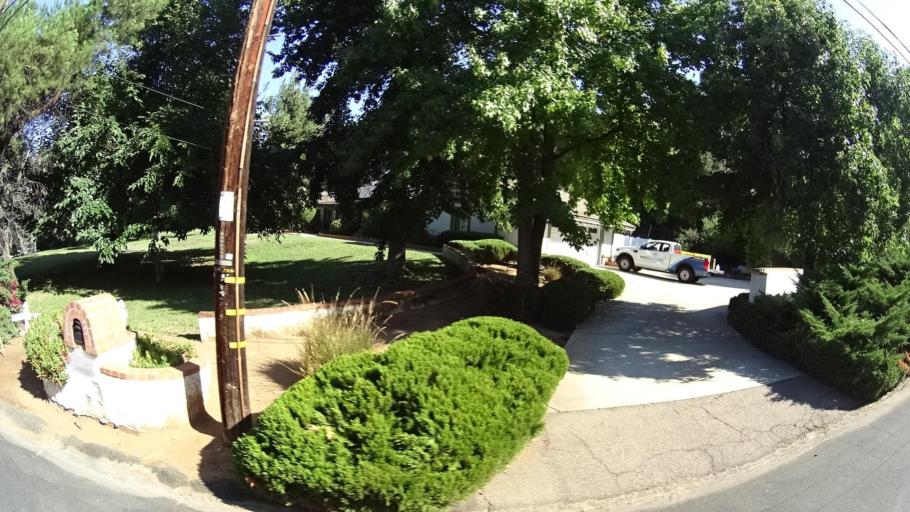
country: US
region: California
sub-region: San Diego County
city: Escondido
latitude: 33.0731
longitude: -117.0828
